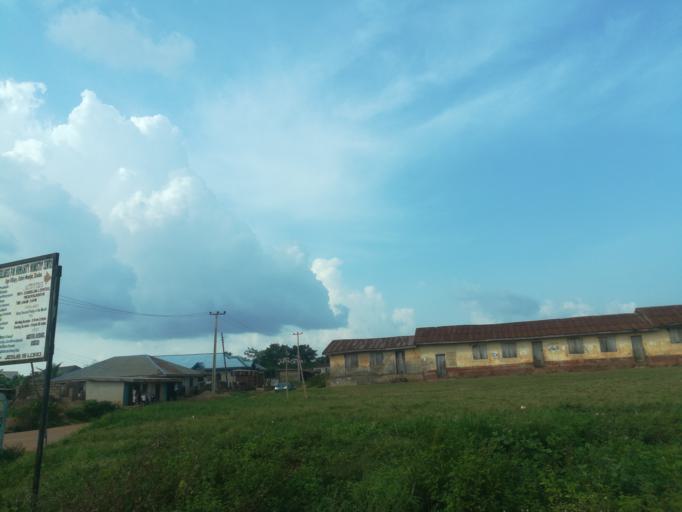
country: NG
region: Oyo
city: Moniya
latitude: 7.5263
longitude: 3.9280
